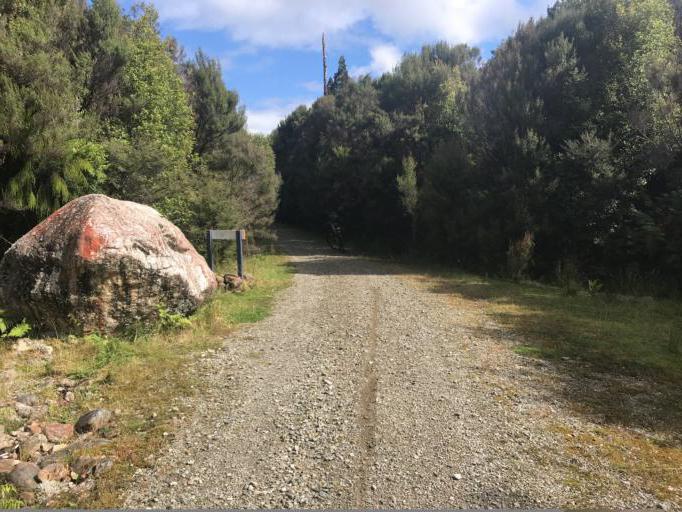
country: NZ
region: West Coast
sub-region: Westland District
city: Hokitika
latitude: -42.7870
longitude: 171.2707
